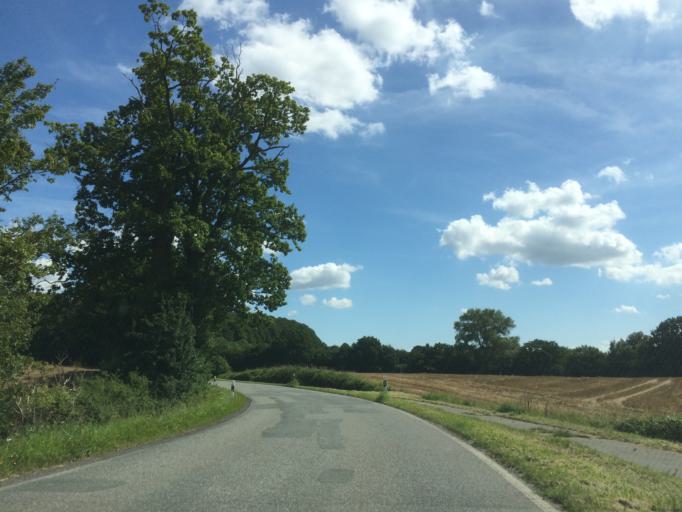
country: DE
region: Schleswig-Holstein
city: Grebin
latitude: 54.1943
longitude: 10.5141
